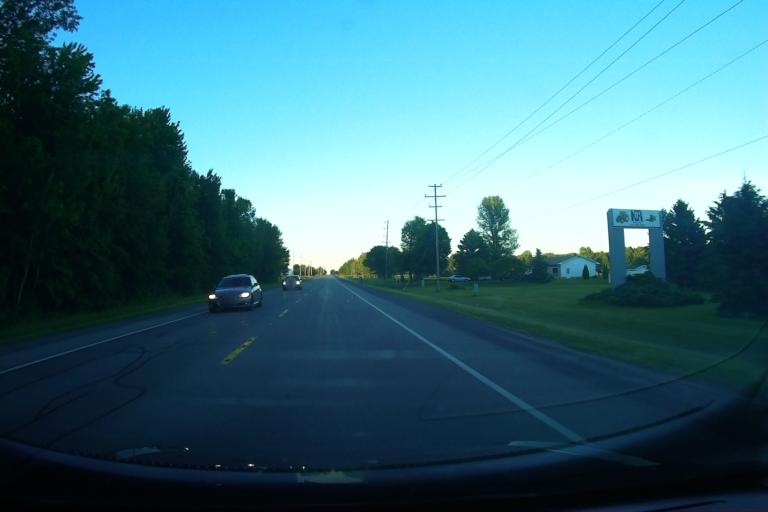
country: CA
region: Ontario
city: Casselman
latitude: 45.0850
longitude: -75.3026
